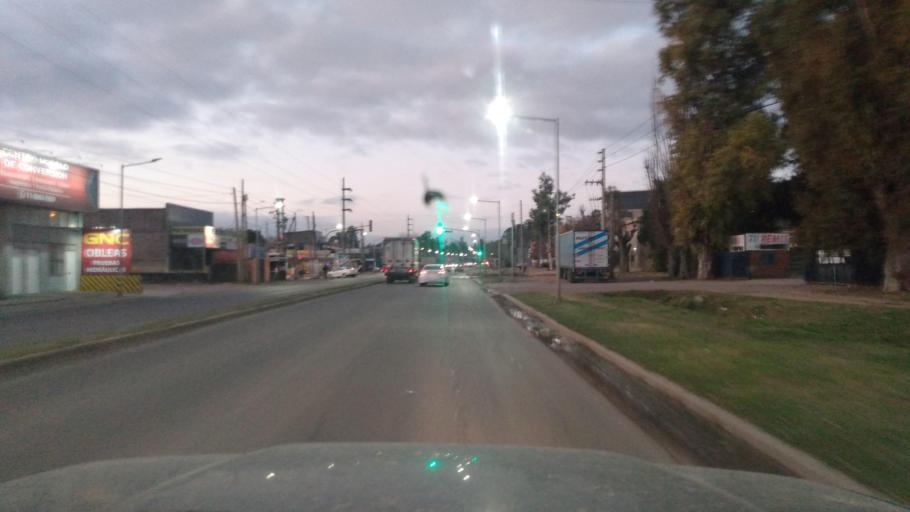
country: AR
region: Buenos Aires
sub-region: Partido de Pilar
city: Pilar
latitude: -34.4463
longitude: -58.9031
